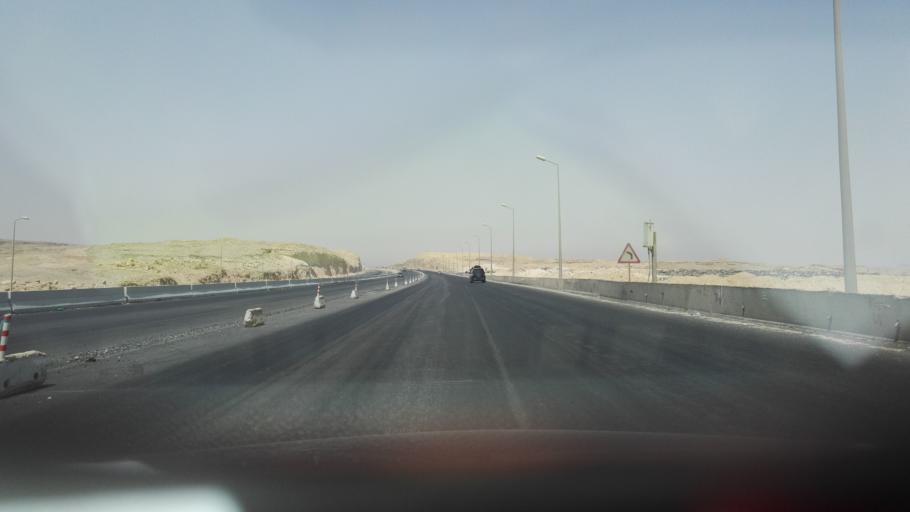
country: EG
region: As Suways
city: Ain Sukhna
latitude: 29.6795
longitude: 32.2214
